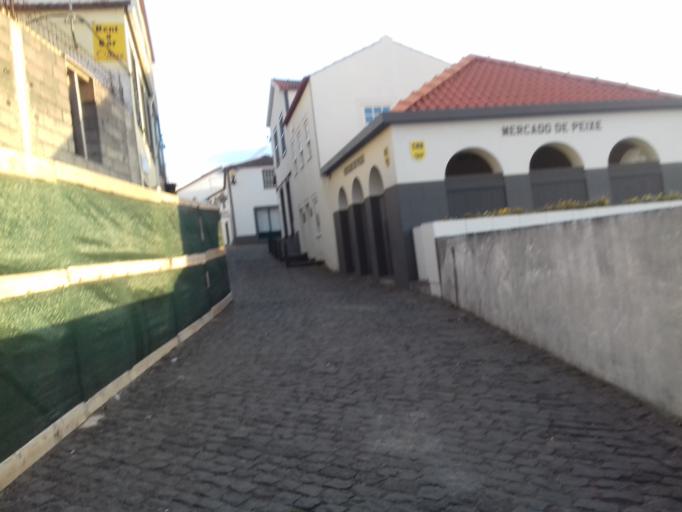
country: PT
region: Azores
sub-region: Madalena
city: Madalena
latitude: 38.5343
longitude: -28.5287
